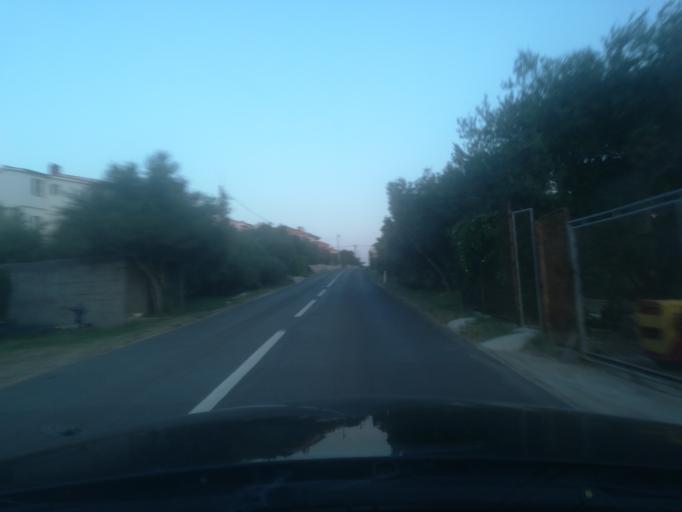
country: HR
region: Primorsko-Goranska
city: Banjol
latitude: 44.7326
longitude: 14.8105
